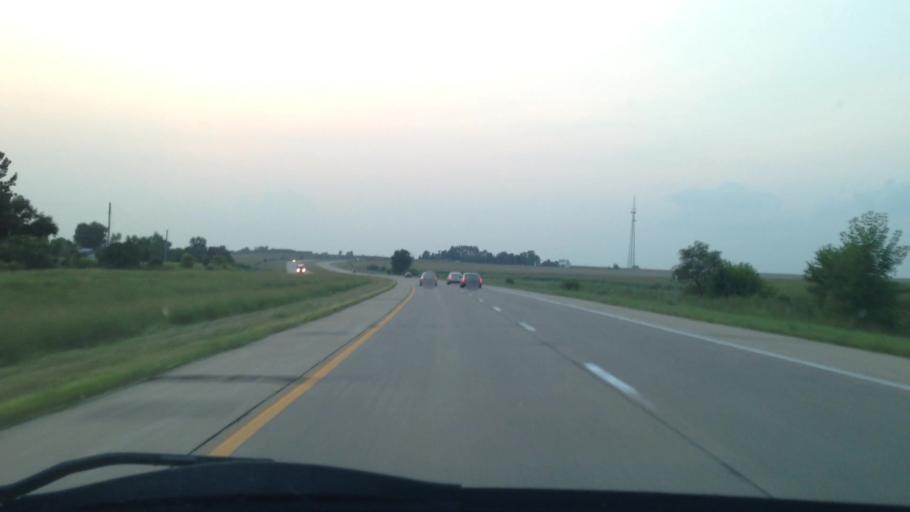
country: US
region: Iowa
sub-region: Benton County
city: Urbana
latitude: 42.2749
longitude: -91.9286
